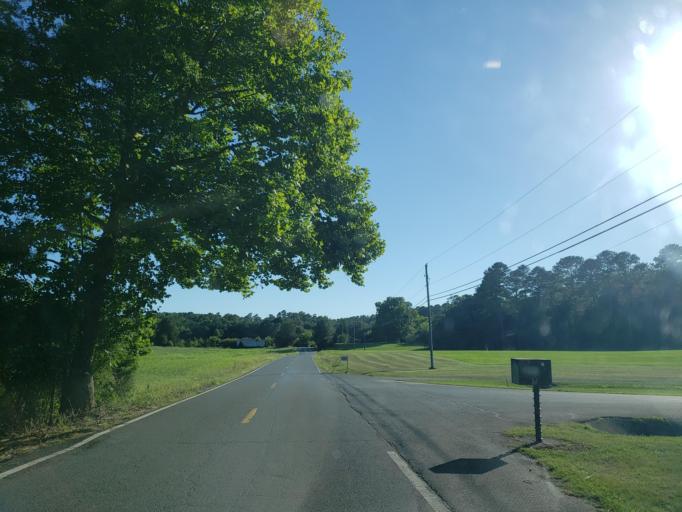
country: US
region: Georgia
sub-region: Floyd County
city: Shannon
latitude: 34.3877
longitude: -85.1189
